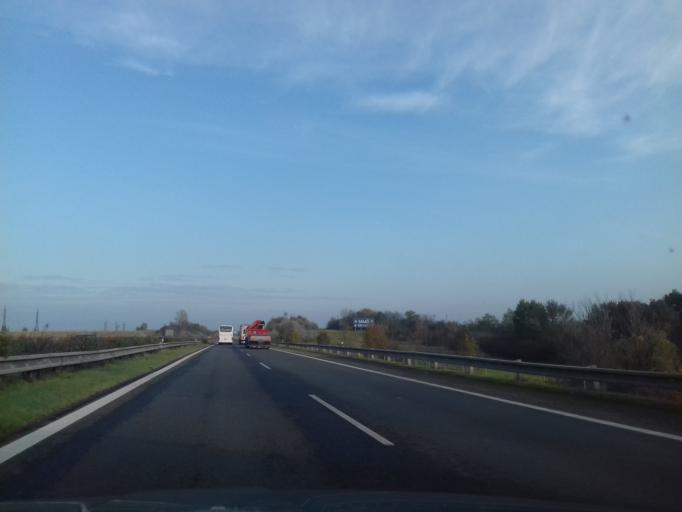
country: SK
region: Bratislavsky
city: Stupava
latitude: 48.2803
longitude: 17.0091
